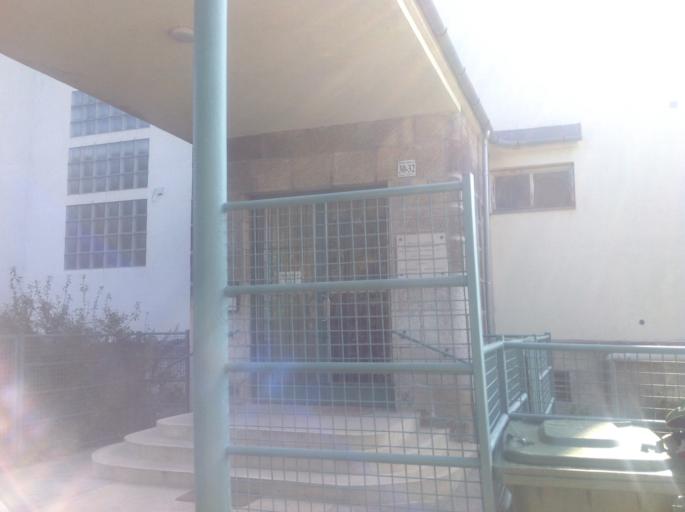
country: HU
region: Budapest
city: Budapest XII. keruelet
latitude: 47.4933
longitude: 18.9797
